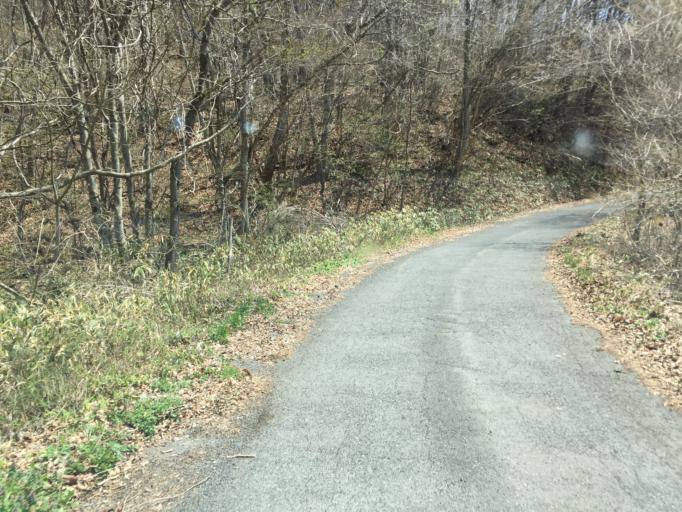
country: JP
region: Fukushima
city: Ishikawa
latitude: 36.9942
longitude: 140.5624
